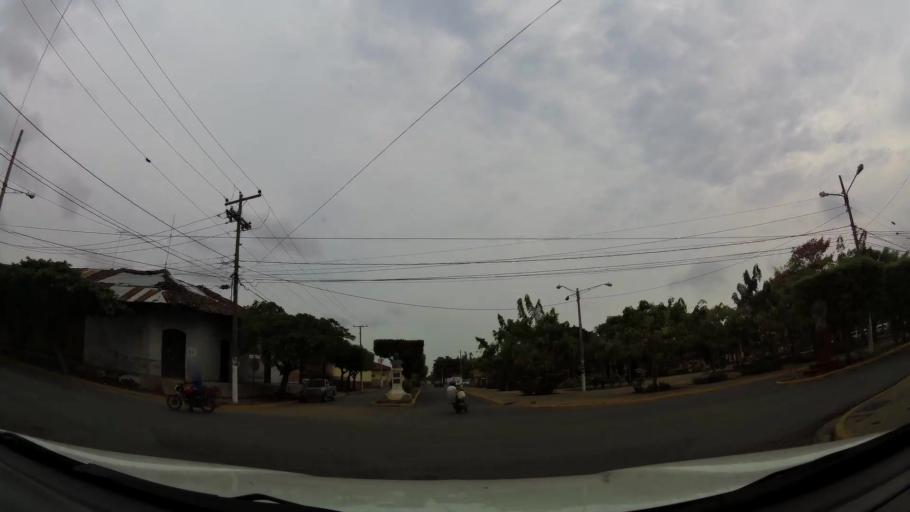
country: NI
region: Granada
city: Granada
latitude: 11.9367
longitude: -85.9563
